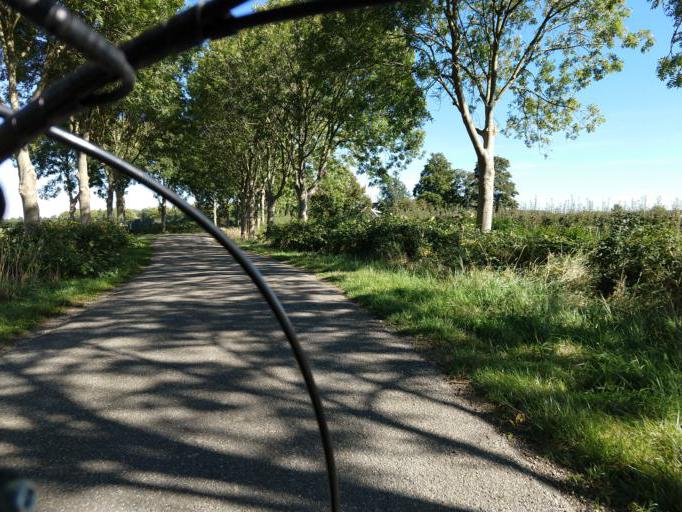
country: NL
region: Zeeland
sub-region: Gemeente Terneuzen
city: Terneuzen
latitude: 51.4115
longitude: 3.8332
